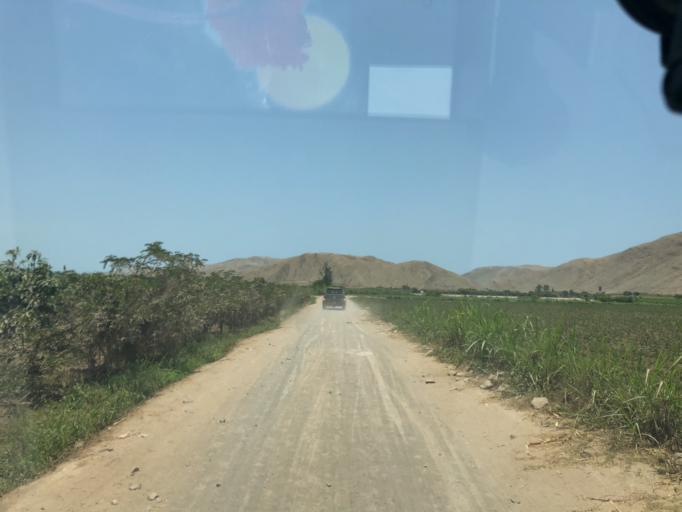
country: PE
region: Lima
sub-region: Provincia de Canete
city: Quilmana
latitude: -12.9710
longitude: -76.4179
